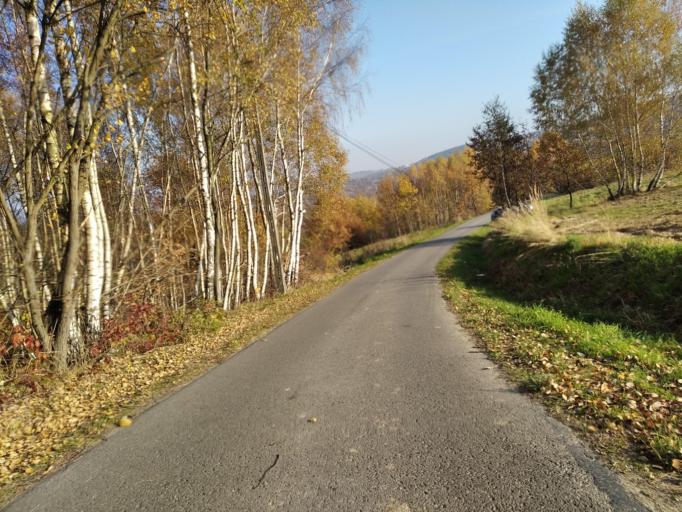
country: PL
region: Subcarpathian Voivodeship
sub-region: Powiat strzyzowski
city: Babica
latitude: 49.9045
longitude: 21.8590
